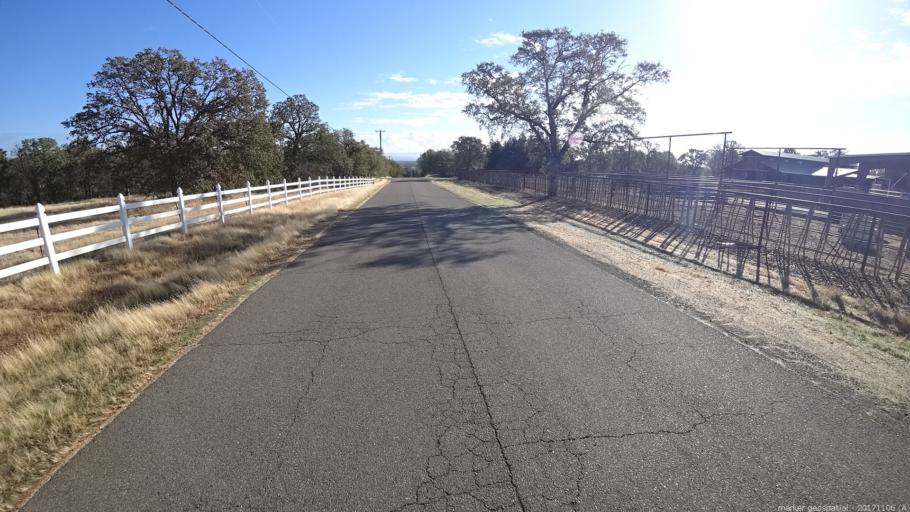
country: US
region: California
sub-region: Shasta County
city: Palo Cedro
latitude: 40.5113
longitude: -122.2481
